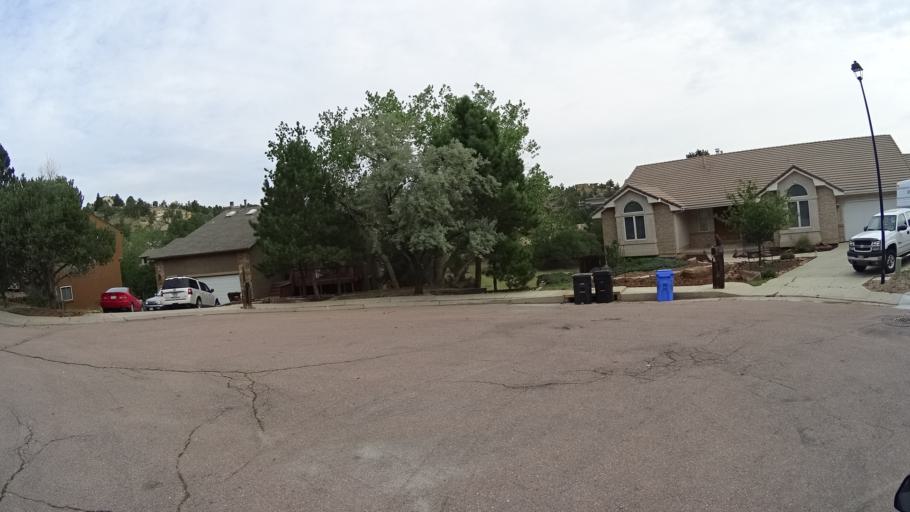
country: US
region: Colorado
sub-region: El Paso County
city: Air Force Academy
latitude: 38.9285
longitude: -104.8502
